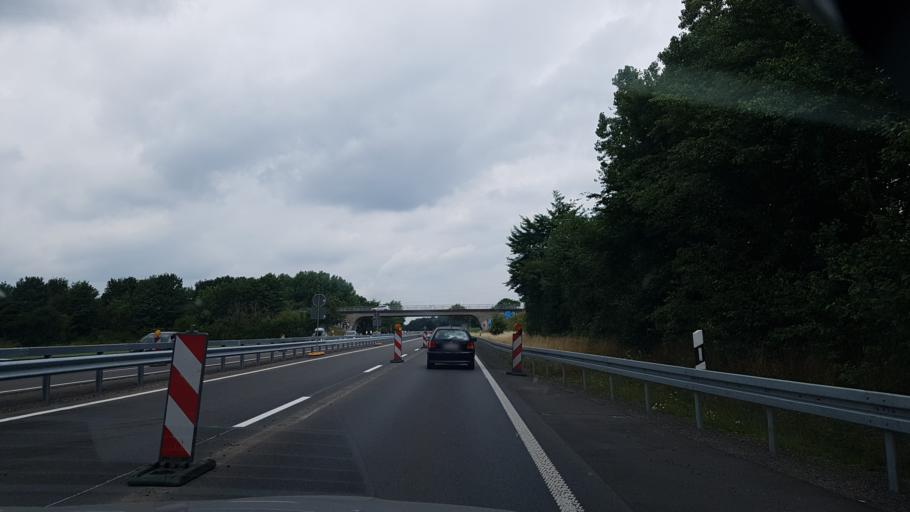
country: DE
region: Schleswig-Holstein
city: Neumunster
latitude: 54.1092
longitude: 9.9692
